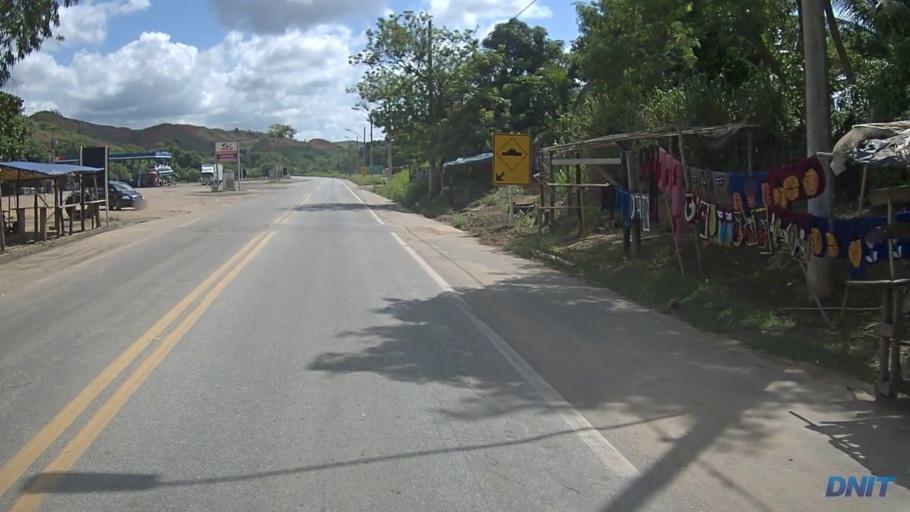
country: BR
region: Minas Gerais
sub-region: Belo Oriente
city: Belo Oriente
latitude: -19.1536
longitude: -42.2353
